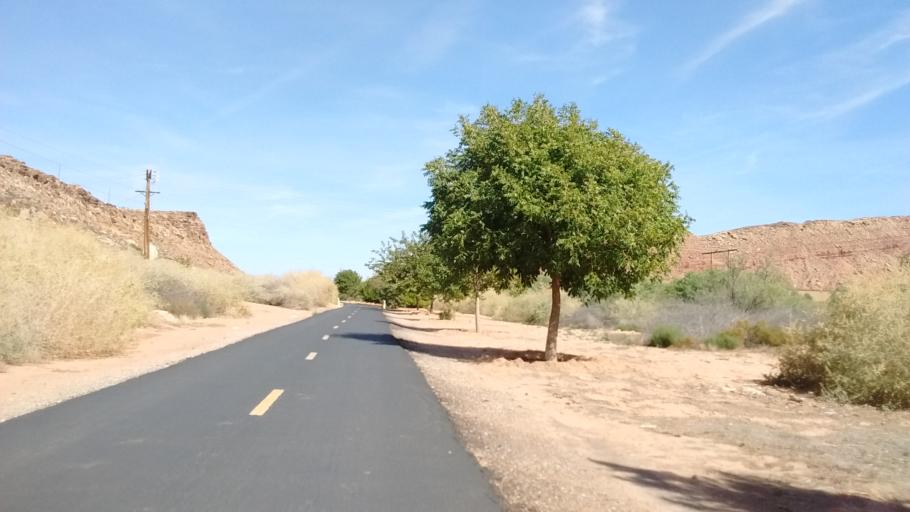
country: US
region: Utah
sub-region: Washington County
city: Saint George
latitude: 37.0639
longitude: -113.5922
